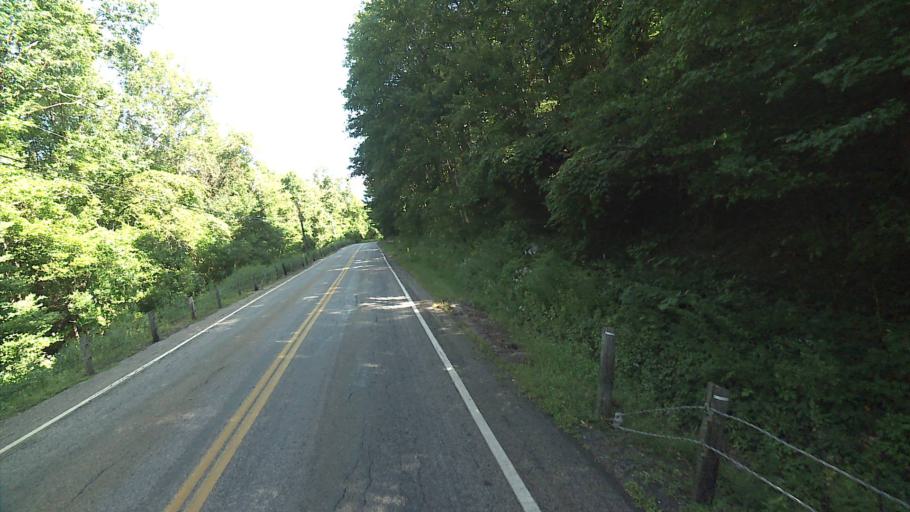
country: US
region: Connecticut
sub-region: Litchfield County
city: Plymouth
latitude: 41.6961
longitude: -73.0575
